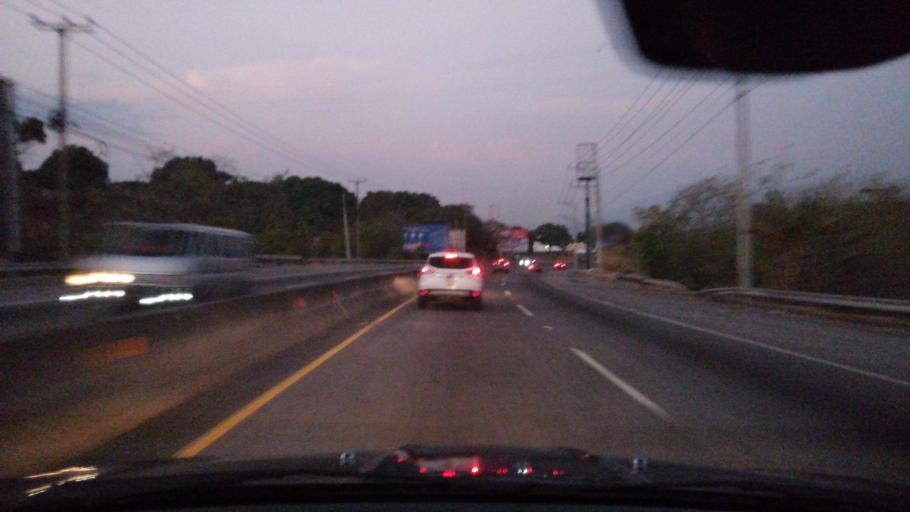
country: SV
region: San Salvador
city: Ayutuxtepeque
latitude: 13.7566
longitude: -89.2162
